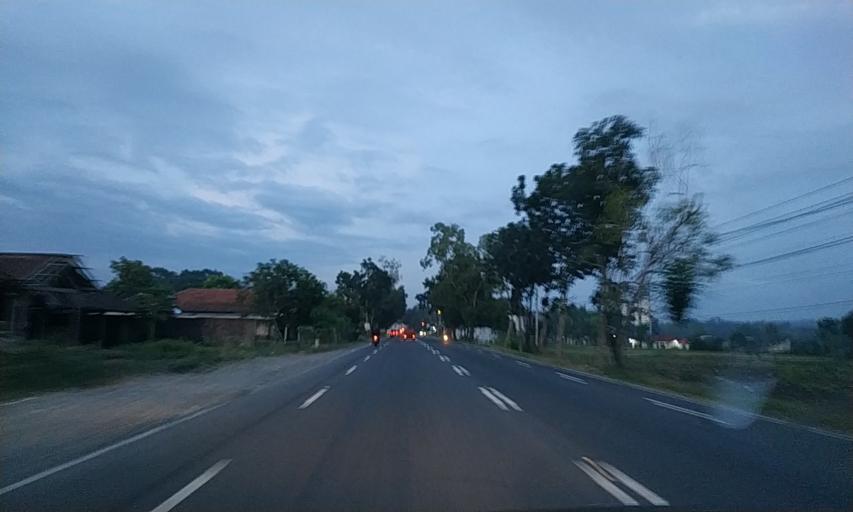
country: ID
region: Daerah Istimewa Yogyakarta
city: Godean
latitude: -7.8251
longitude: 110.2287
